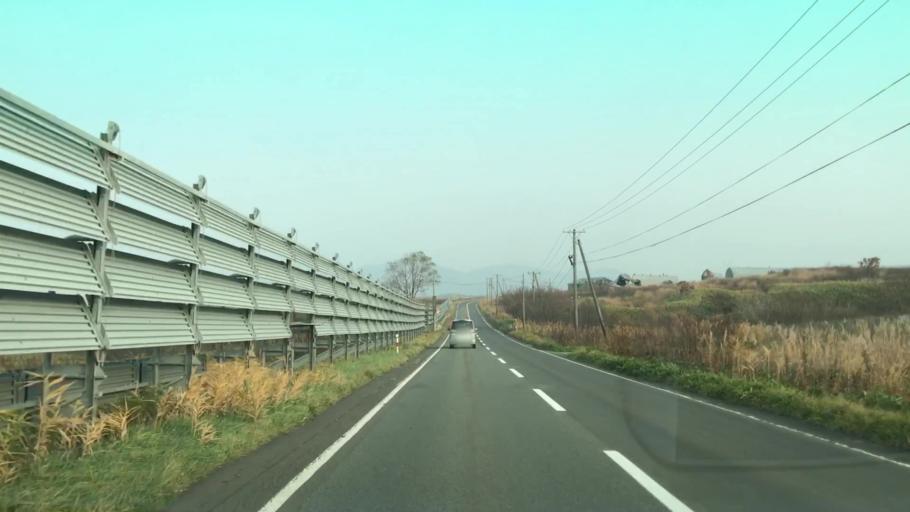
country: JP
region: Hokkaido
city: Ishikari
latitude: 43.3462
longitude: 141.4242
